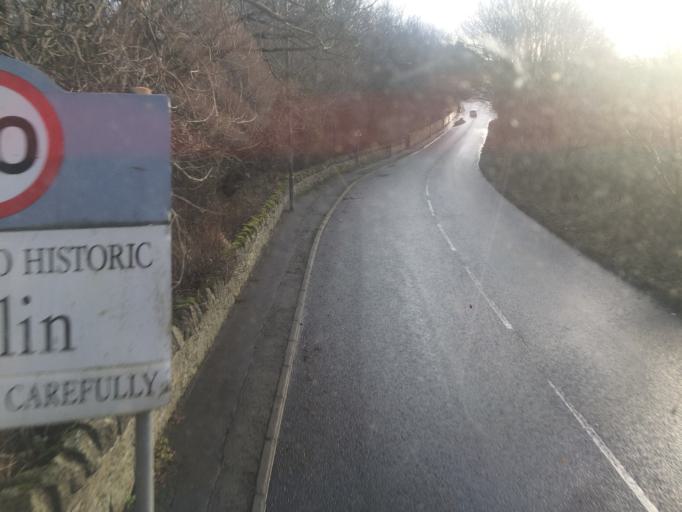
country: GB
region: Scotland
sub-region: Midlothian
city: Loanhead
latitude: 55.8634
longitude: -3.1704
